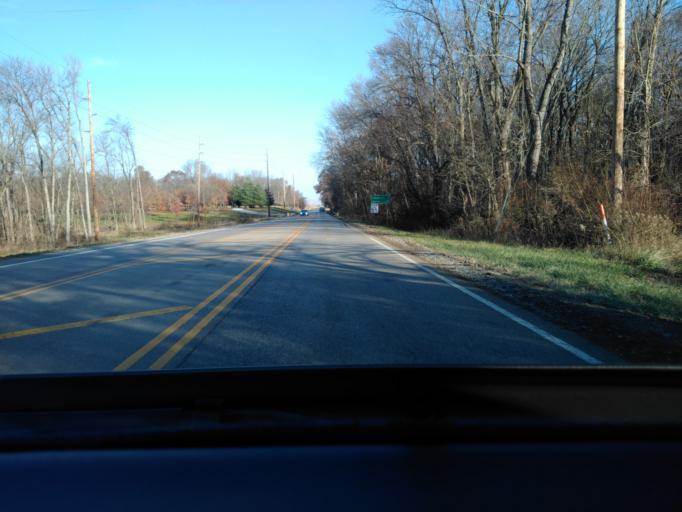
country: US
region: Illinois
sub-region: Madison County
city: Saint Jacob
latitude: 38.7202
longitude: -89.8011
